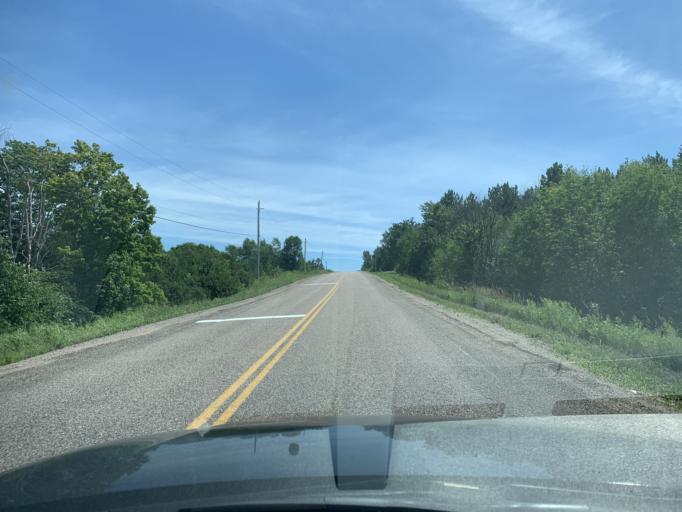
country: CA
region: Ontario
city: Pembroke
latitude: 45.4413
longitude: -77.2957
